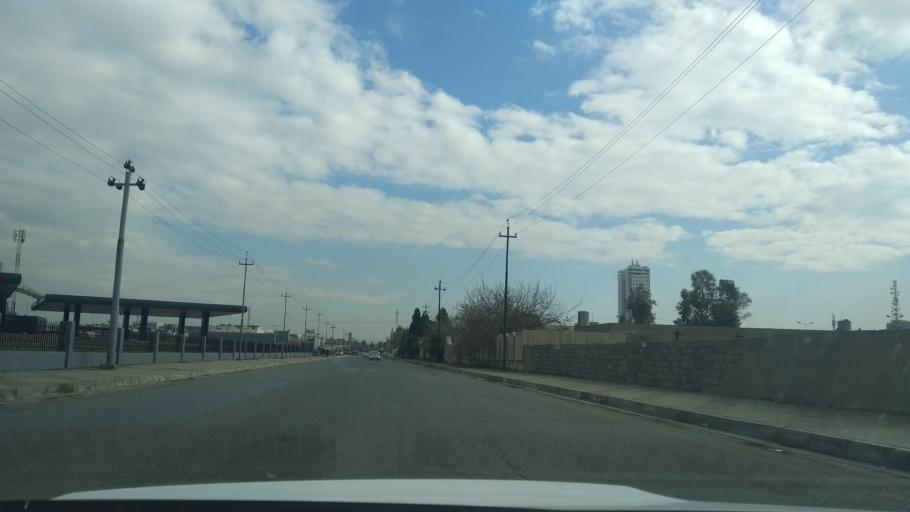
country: IQ
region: Arbil
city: Erbil
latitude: 36.1846
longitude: 43.9864
